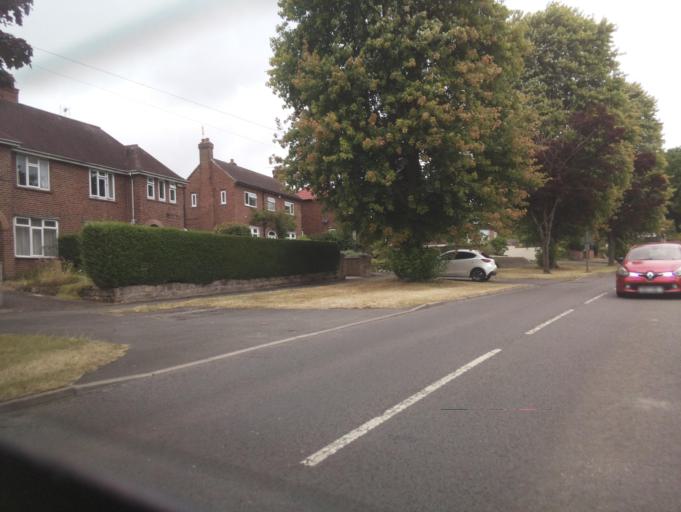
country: GB
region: England
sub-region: Derby
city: Derby
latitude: 52.9010
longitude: -1.5104
